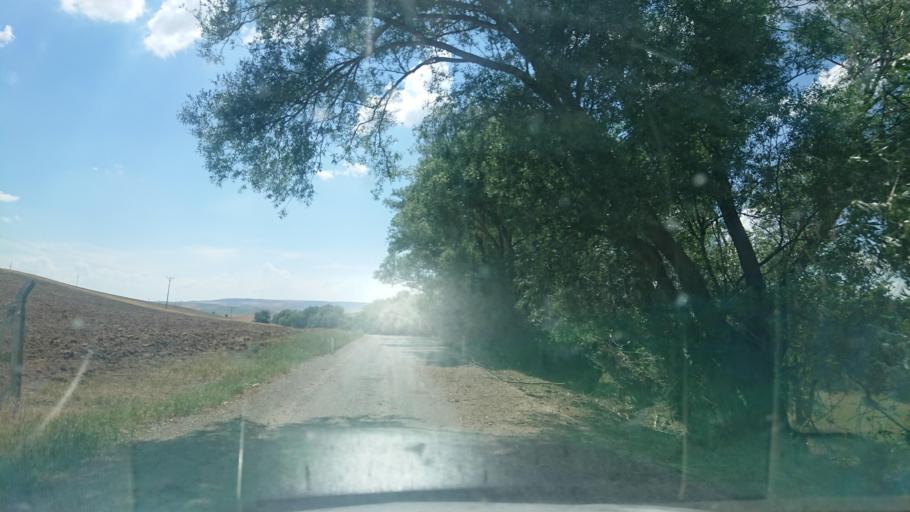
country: TR
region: Aksaray
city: Agacoren
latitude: 38.8368
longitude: 33.8070
